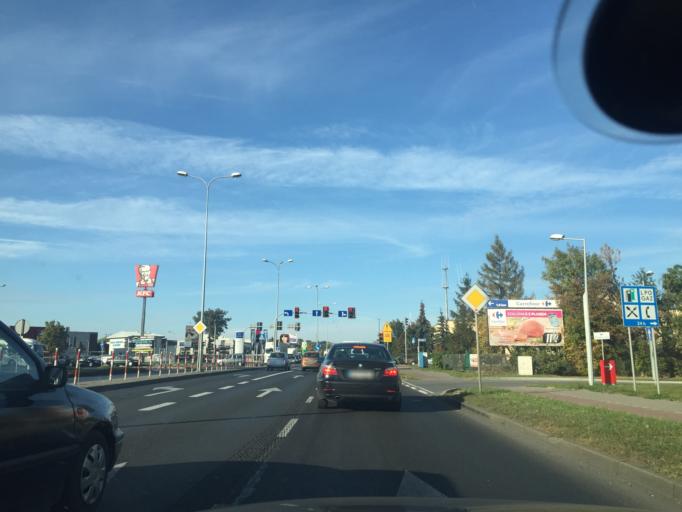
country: PL
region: Kujawsko-Pomorskie
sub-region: Powiat inowroclawski
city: Inowroclaw
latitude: 52.7785
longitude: 18.2598
